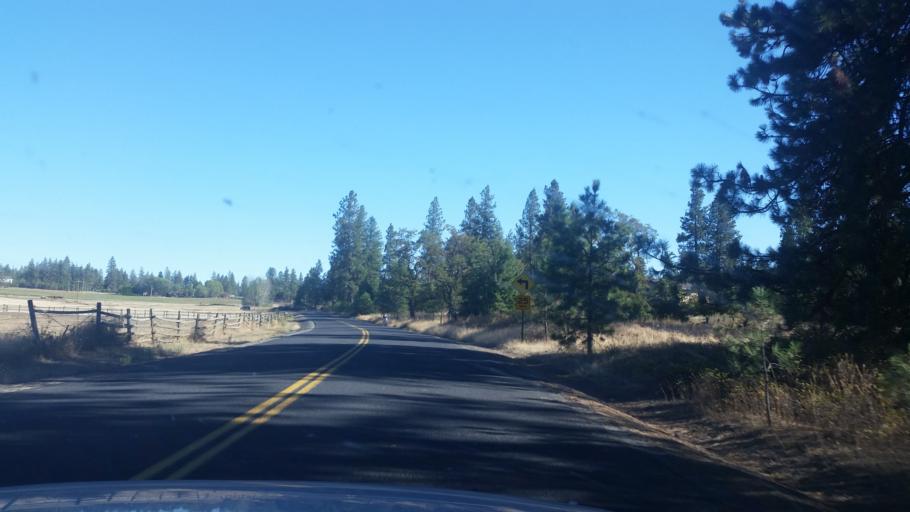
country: US
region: Washington
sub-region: Spokane County
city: Cheney
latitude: 47.5383
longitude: -117.4753
